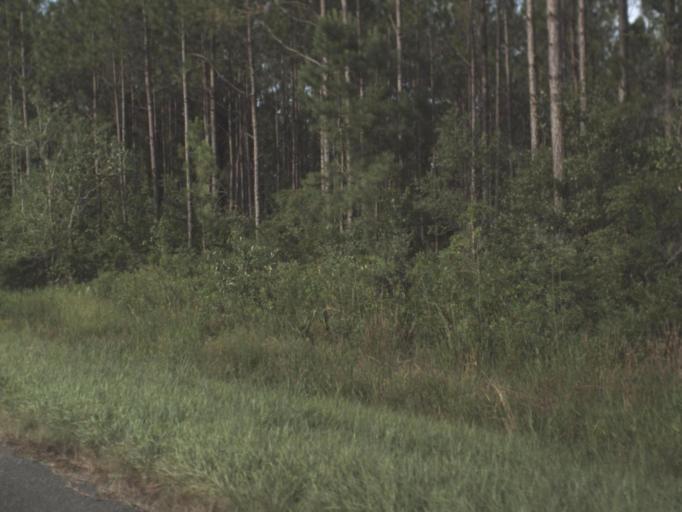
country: US
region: Florida
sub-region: Taylor County
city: Perry
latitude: 30.2244
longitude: -83.6156
